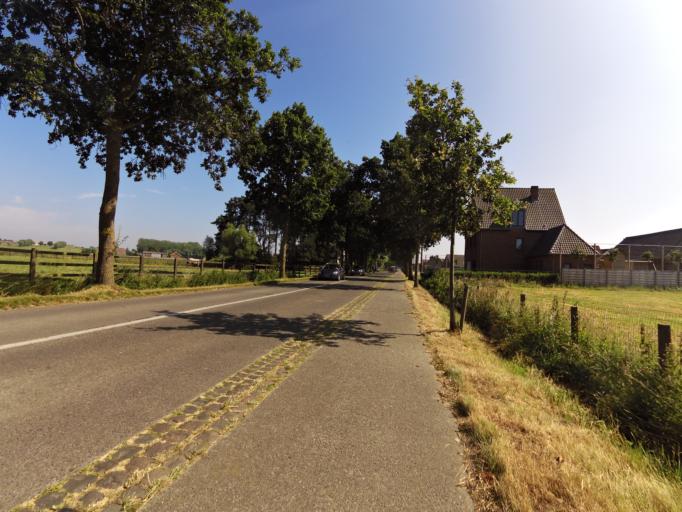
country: BE
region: Flanders
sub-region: Provincie West-Vlaanderen
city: Jabbeke
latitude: 51.1300
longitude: 3.0834
